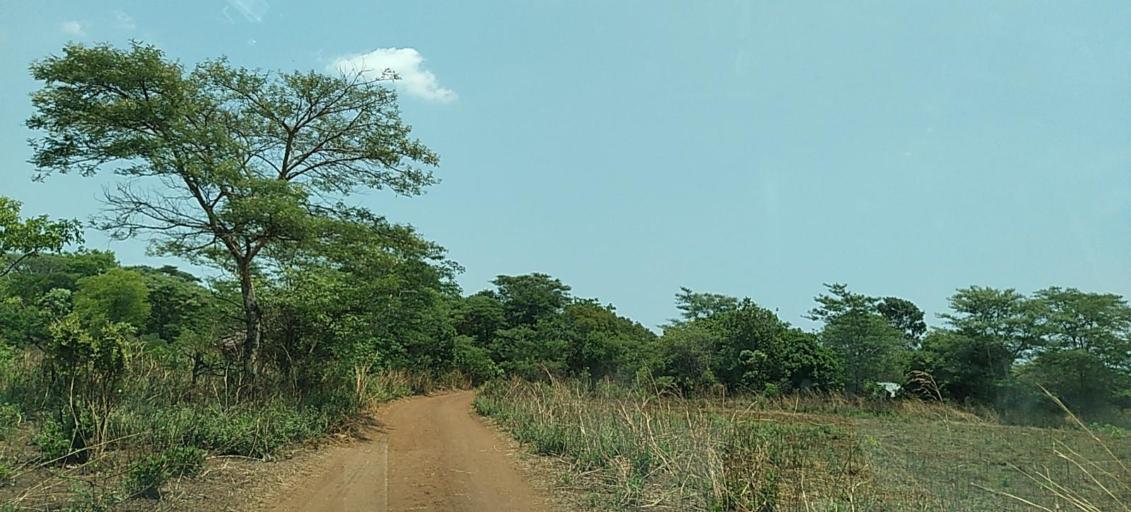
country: ZM
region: Copperbelt
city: Mpongwe
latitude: -13.8364
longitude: 27.8386
